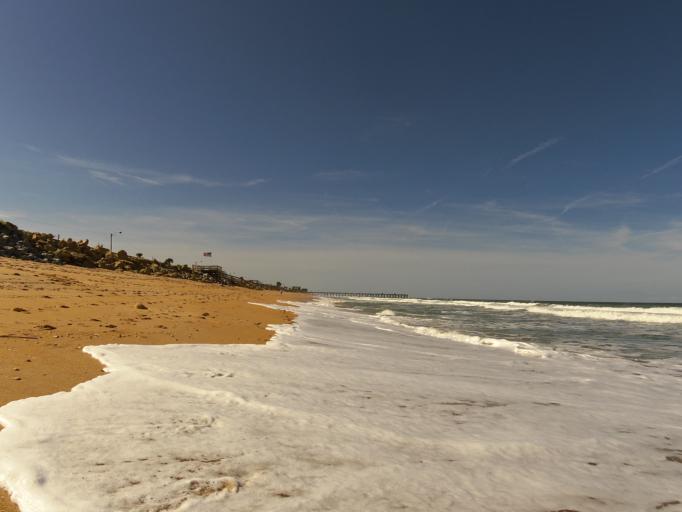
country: US
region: Florida
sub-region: Flagler County
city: Flagler Beach
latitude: 29.4732
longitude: -81.1233
